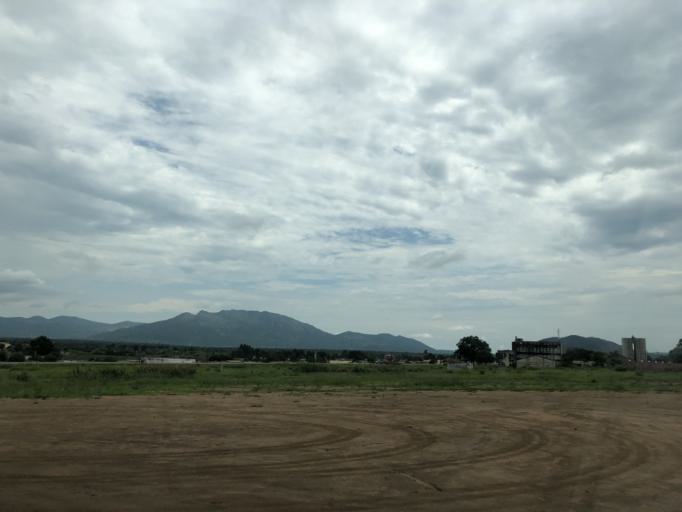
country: AO
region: Cuanza Sul
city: Quibala
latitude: -10.7281
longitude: 14.9714
